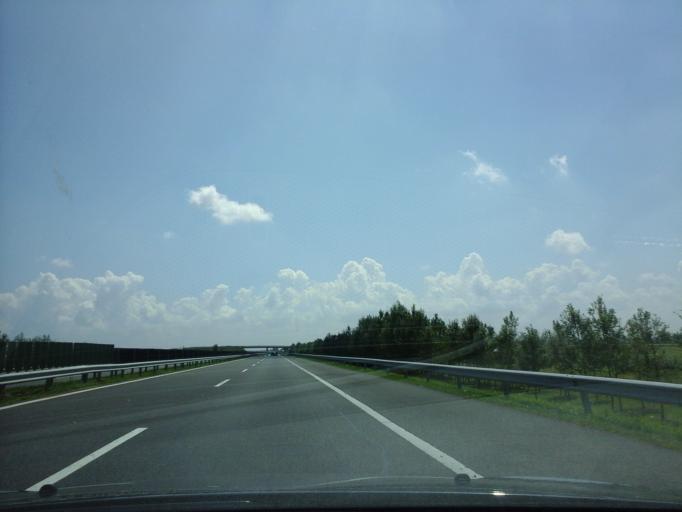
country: HU
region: Hajdu-Bihar
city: Hajduboszormeny
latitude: 47.6837
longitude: 21.4516
